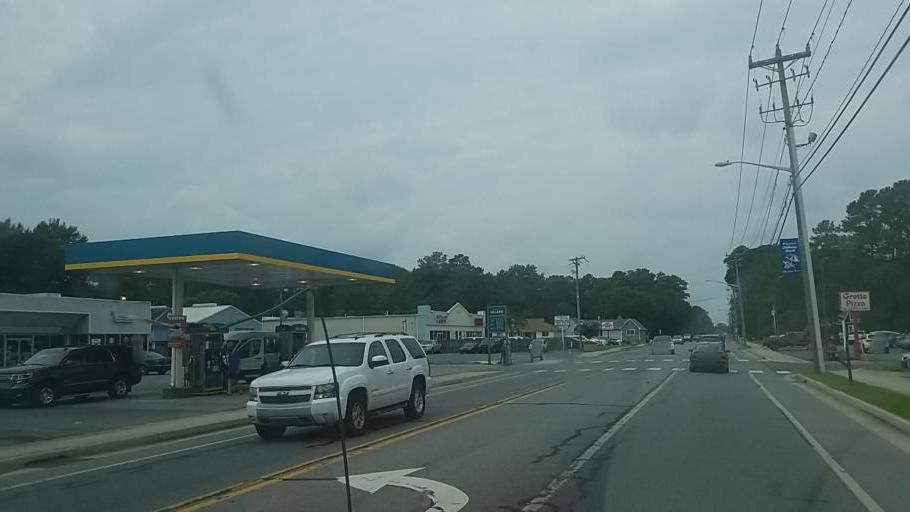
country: US
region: Delaware
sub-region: Sussex County
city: Bethany Beach
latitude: 38.5404
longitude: -75.0713
